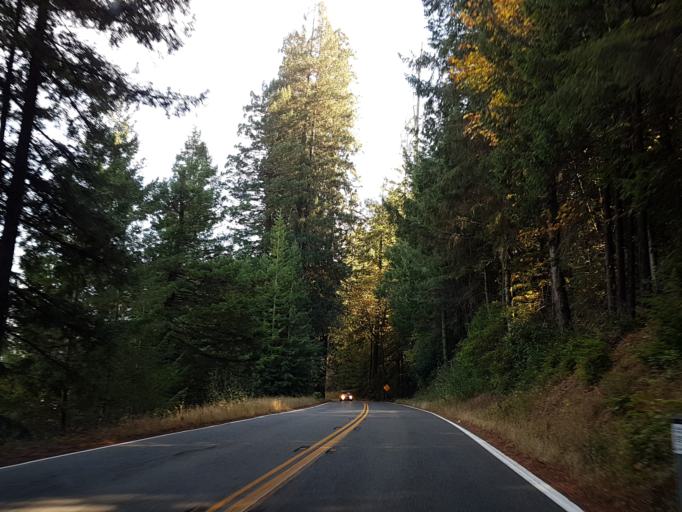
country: US
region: California
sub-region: Humboldt County
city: Rio Dell
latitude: 40.4282
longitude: -123.9828
